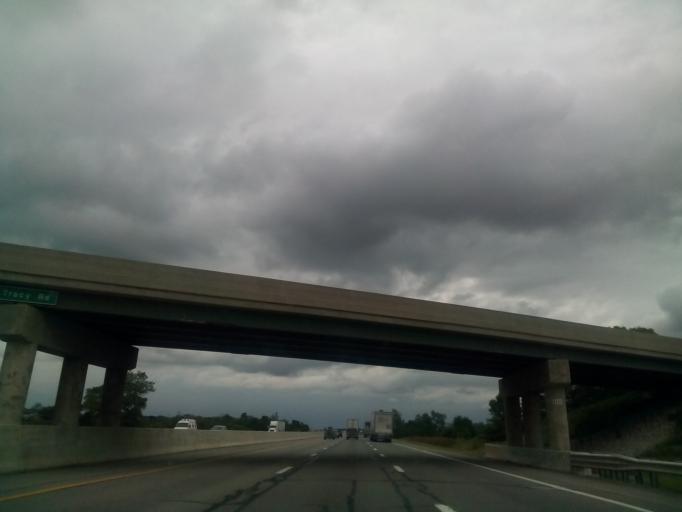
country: US
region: Ohio
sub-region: Wood County
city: Walbridge
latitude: 41.5447
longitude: -83.5290
